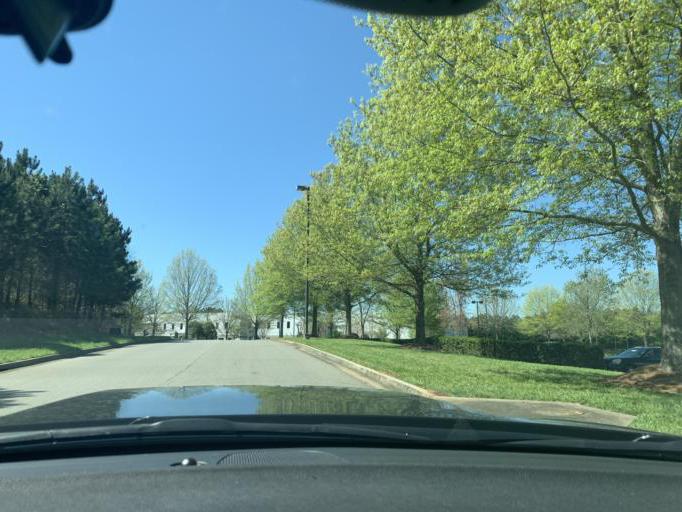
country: US
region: Georgia
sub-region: Fulton County
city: Johns Creek
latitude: 34.1211
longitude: -84.2082
